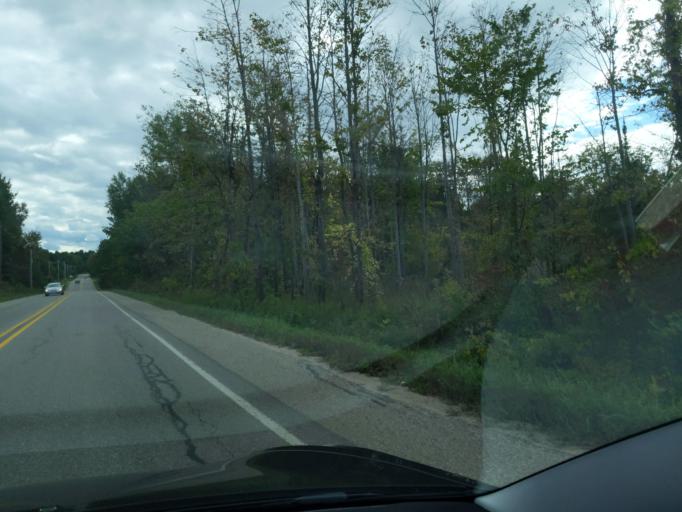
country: US
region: Michigan
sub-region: Kalkaska County
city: Rapid City
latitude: 44.8917
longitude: -85.2723
